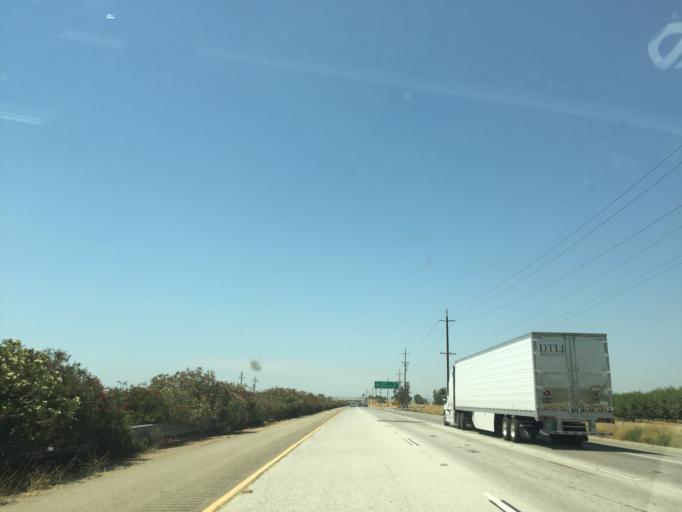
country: US
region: California
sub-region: Kern County
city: Weedpatch
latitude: 35.0496
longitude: -118.9652
